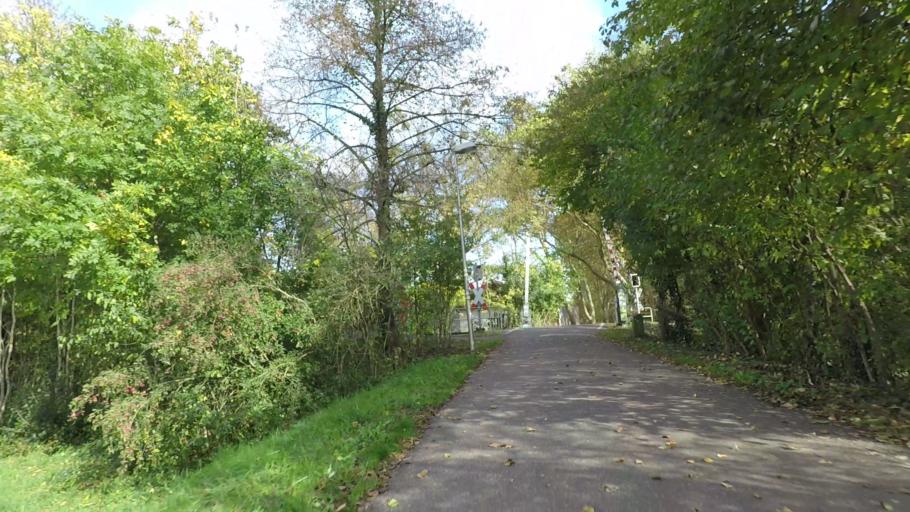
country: DE
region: Baden-Wuerttemberg
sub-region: Tuebingen Region
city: Tuebingen
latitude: 48.5127
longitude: 9.0423
